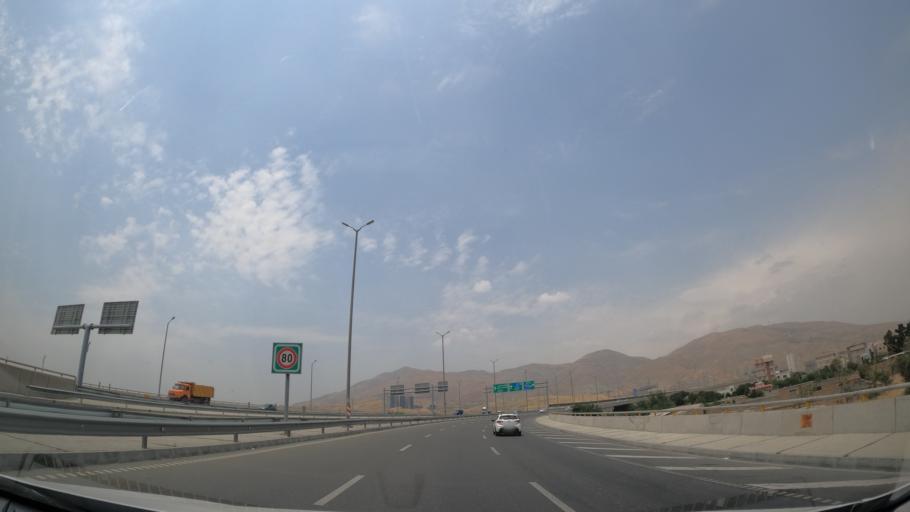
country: IR
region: Tehran
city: Shahr-e Qods
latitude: 35.7365
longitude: 51.1217
